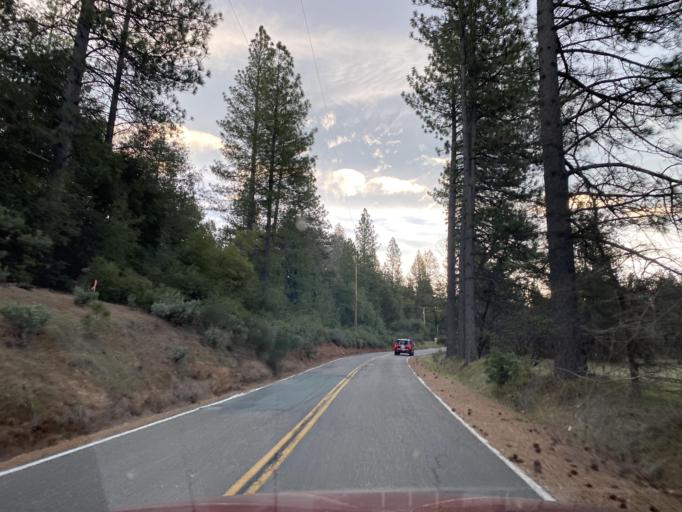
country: US
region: California
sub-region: Amador County
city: Pine Grove
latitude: 38.5016
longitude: -120.6544
